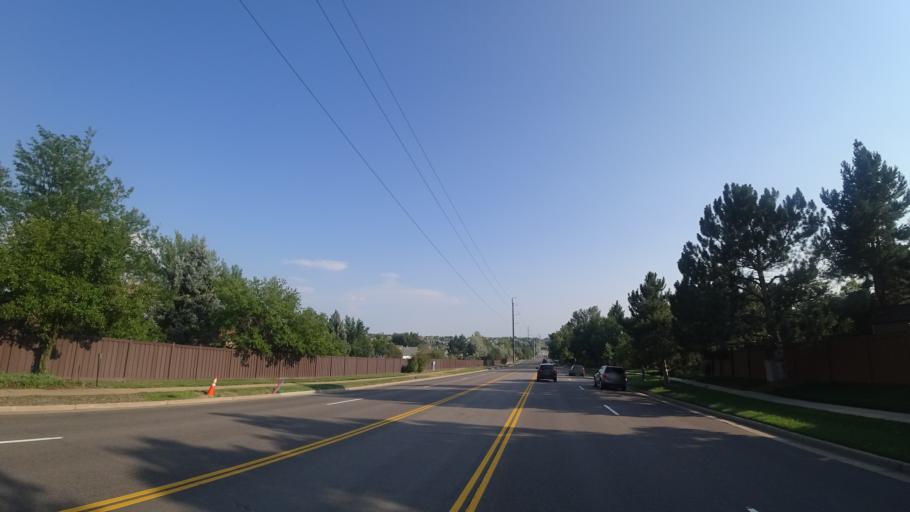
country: US
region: Colorado
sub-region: Arapahoe County
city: Dove Valley
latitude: 39.6170
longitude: -104.7917
